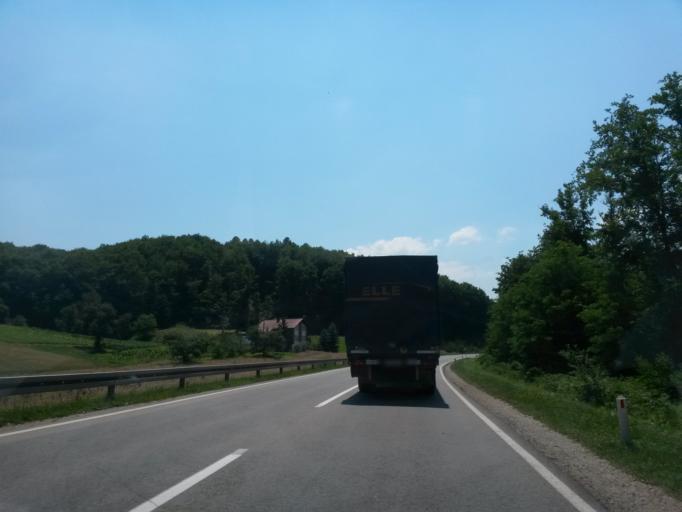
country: BA
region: Federation of Bosnia and Herzegovina
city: Lijesnica
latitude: 44.4726
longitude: 18.0692
